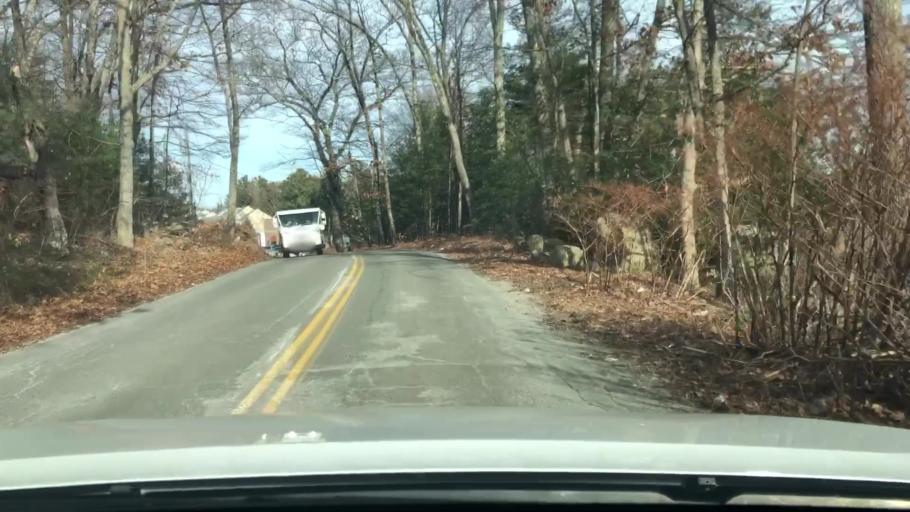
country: US
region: Massachusetts
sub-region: Worcester County
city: Milford
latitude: 42.1202
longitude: -71.4959
